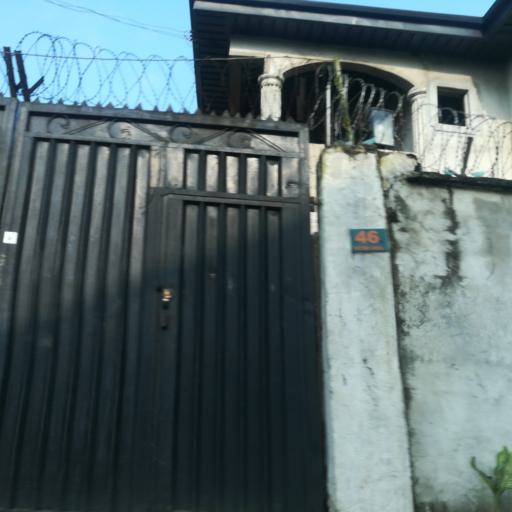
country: NG
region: Rivers
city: Port Harcourt
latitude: 4.8521
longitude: 6.9599
